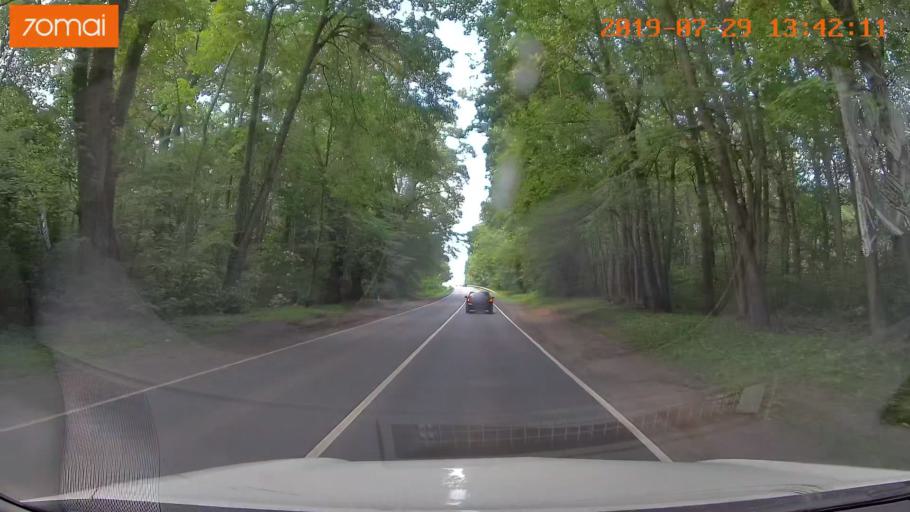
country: RU
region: Kaliningrad
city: Svetlyy
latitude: 54.7366
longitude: 20.1162
